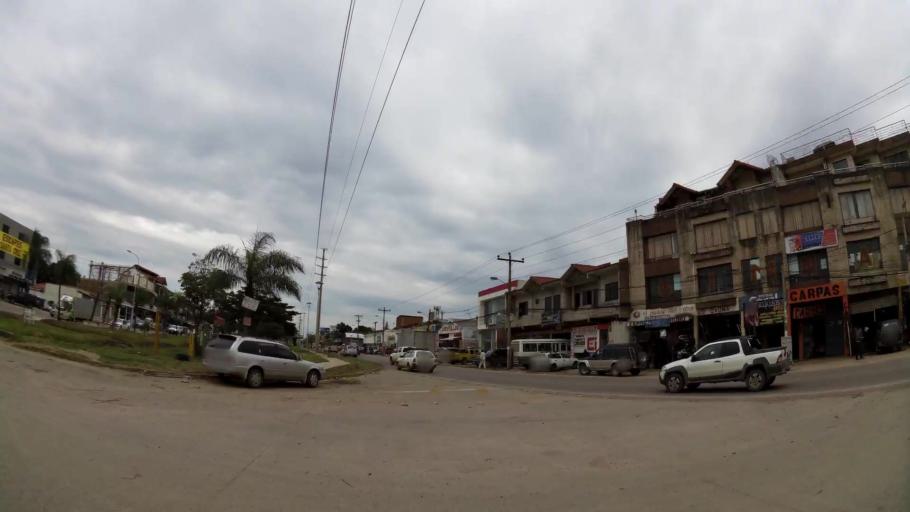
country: BO
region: Santa Cruz
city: Santa Cruz de la Sierra
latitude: -17.7506
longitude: -63.1874
